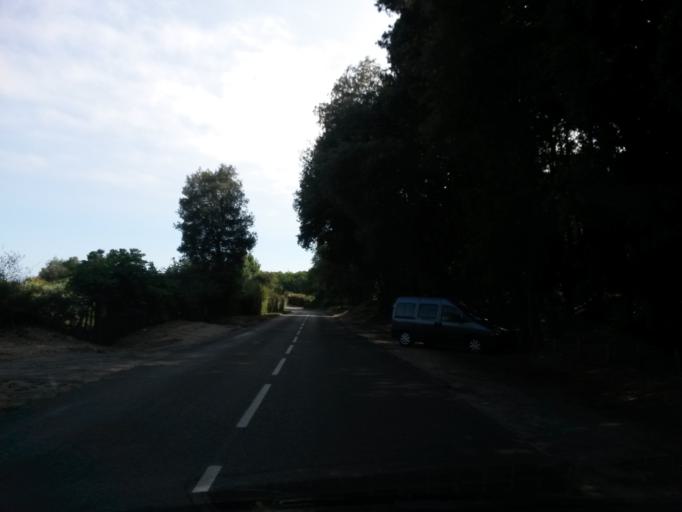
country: FR
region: Pays de la Loire
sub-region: Departement de la Vendee
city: Les Sables-d'Olonne
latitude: 46.5272
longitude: -1.8106
